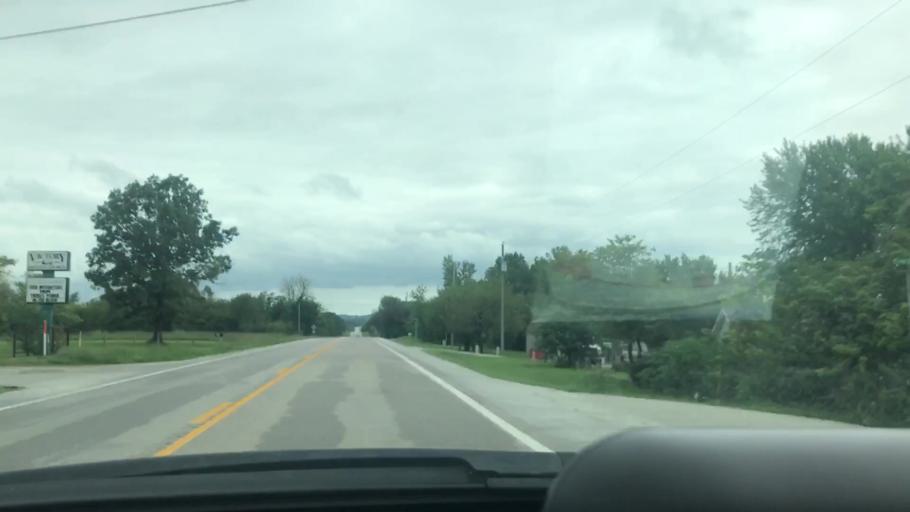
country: US
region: Missouri
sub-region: Dallas County
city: Buffalo
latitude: 37.7058
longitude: -93.1110
